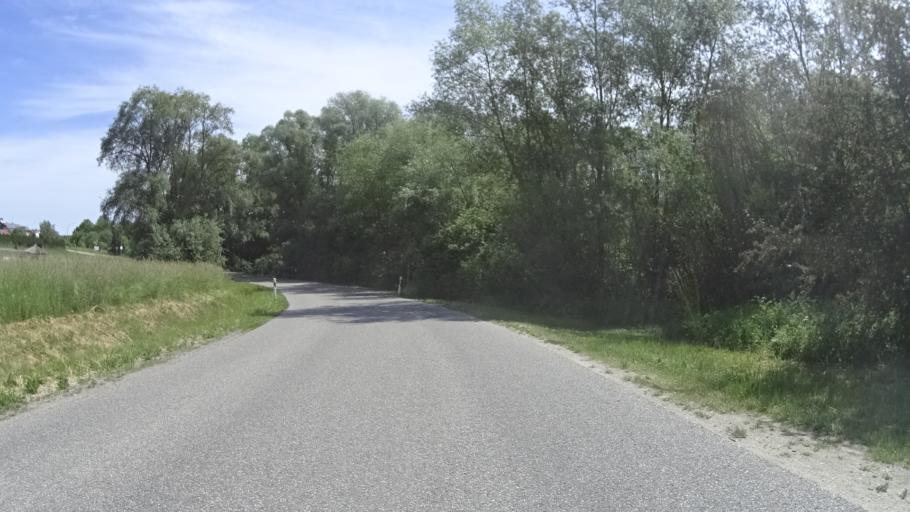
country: DE
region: Bavaria
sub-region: Lower Bavaria
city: Bad Abbach
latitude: 48.9287
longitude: 12.0106
